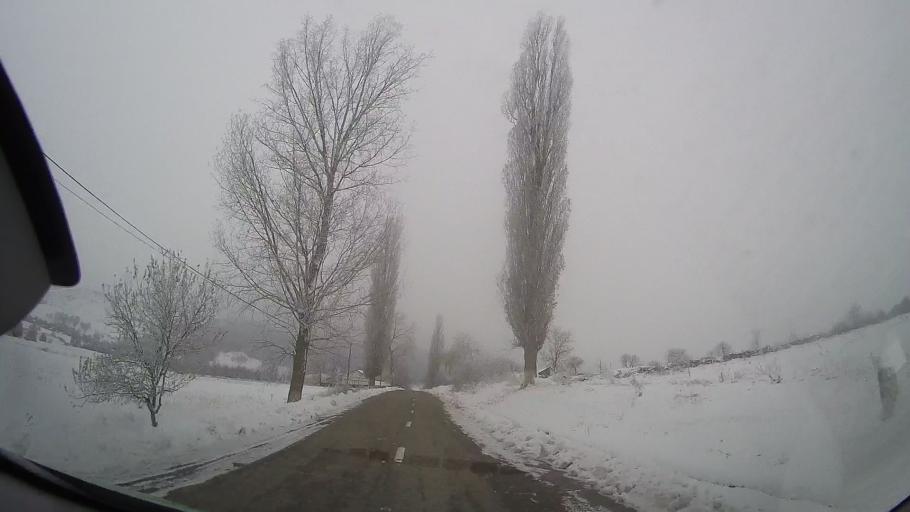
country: RO
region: Neamt
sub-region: Comuna Bozieni
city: Bozieni
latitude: 46.8405
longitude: 27.1677
